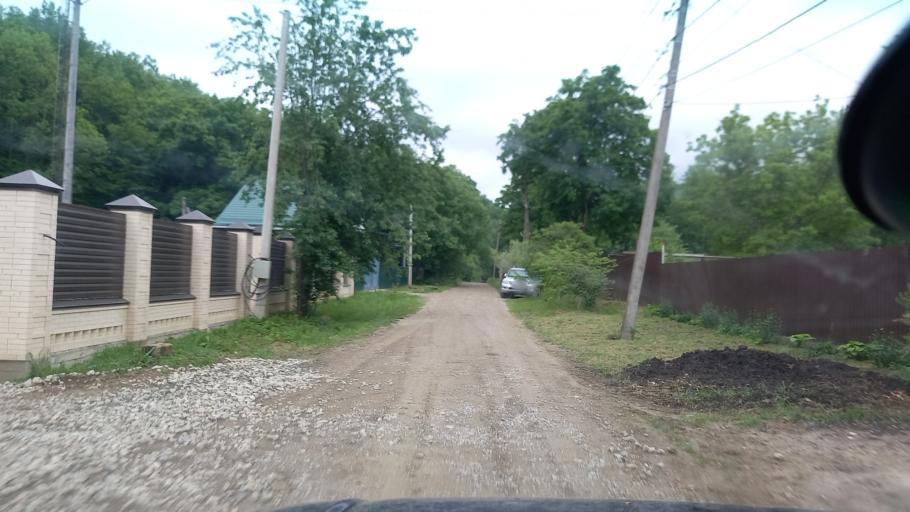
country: RU
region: Krasnodarskiy
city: Azovskaya
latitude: 44.6368
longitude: 38.6185
